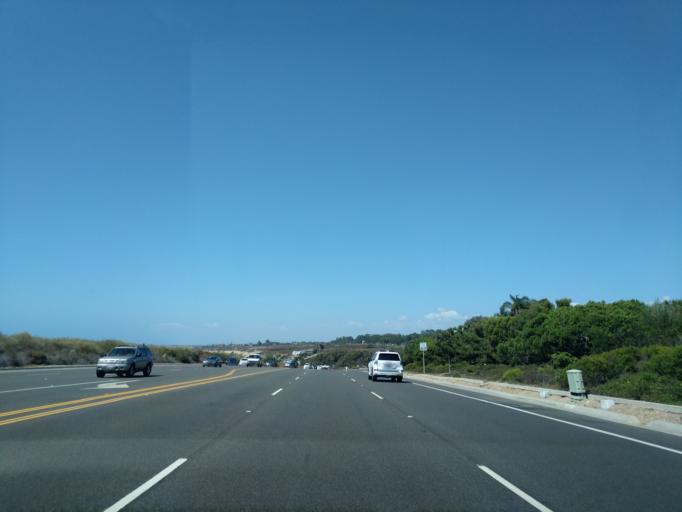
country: US
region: California
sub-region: Orange County
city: San Joaquin Hills
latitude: 33.5718
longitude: -117.8367
